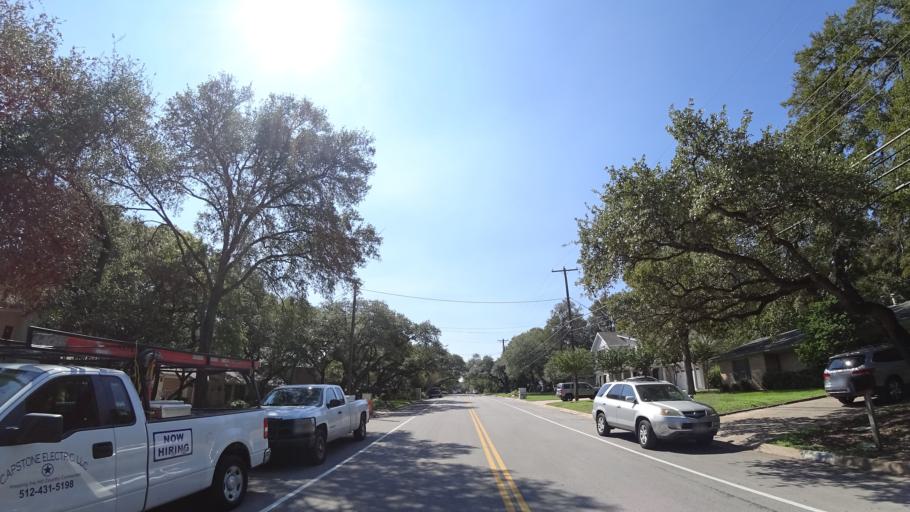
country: US
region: Texas
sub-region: Travis County
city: Rollingwood
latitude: 30.2786
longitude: -97.7902
